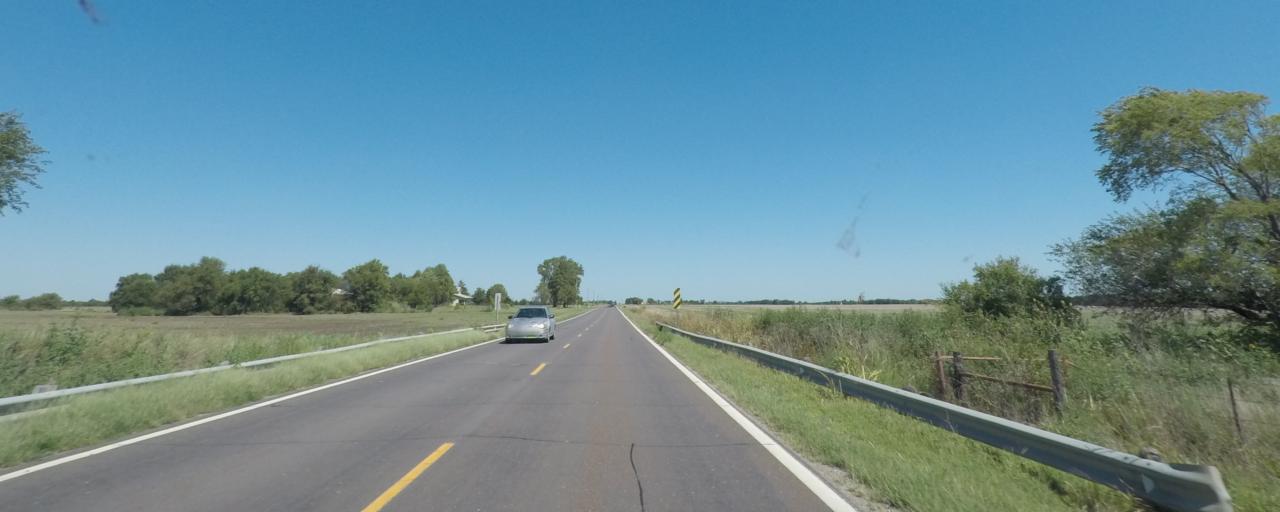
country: US
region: Kansas
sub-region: Sumner County
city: Wellington
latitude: 37.1366
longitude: -97.4021
